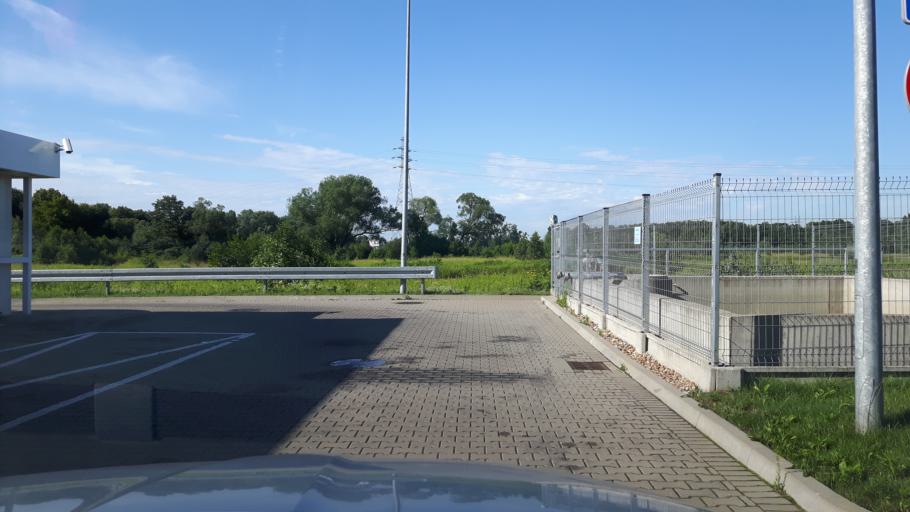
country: PL
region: Masovian Voivodeship
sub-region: Powiat wolominski
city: Zabki
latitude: 52.2989
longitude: 21.0838
